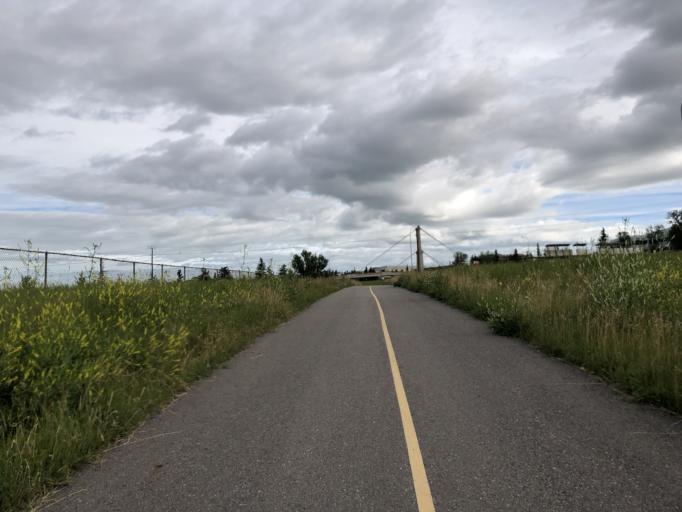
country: CA
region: Alberta
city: Calgary
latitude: 51.0730
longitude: -114.0279
